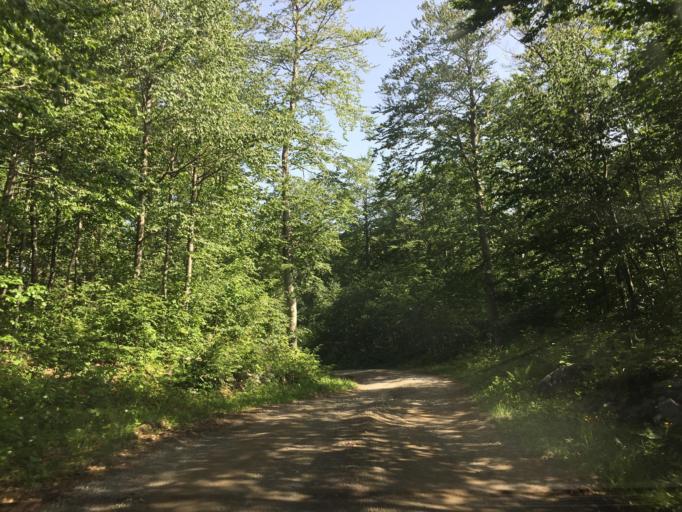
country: HR
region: Primorsko-Goranska
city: Podhum
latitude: 45.4320
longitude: 14.5790
